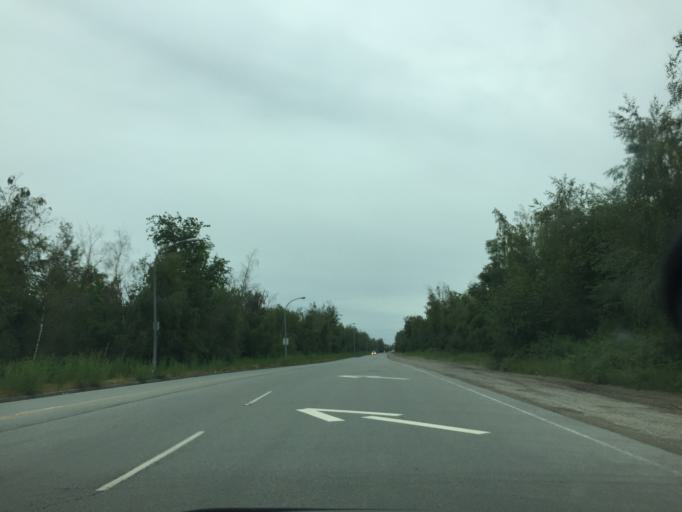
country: CA
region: British Columbia
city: Richmond
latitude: 49.1762
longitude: -123.1031
